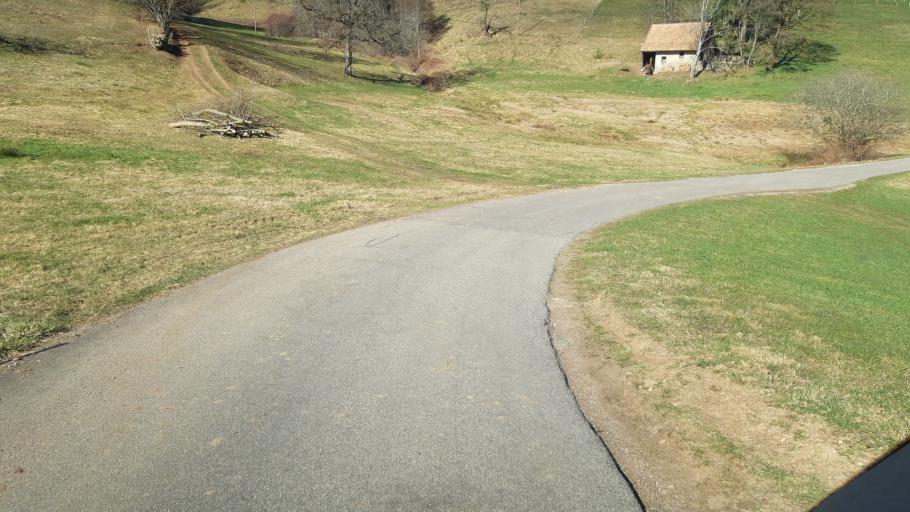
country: DE
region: Baden-Wuerttemberg
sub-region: Freiburg Region
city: Gutach im Breisgau
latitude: 48.1746
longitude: 7.9859
